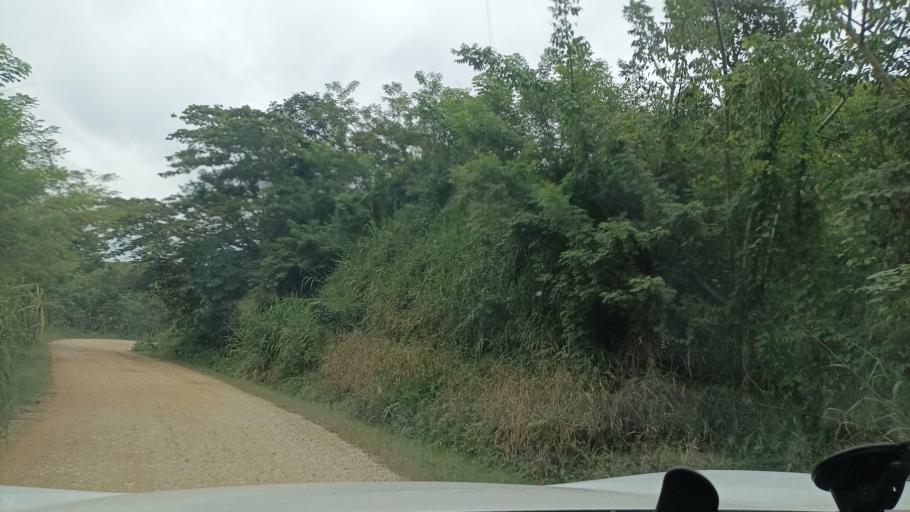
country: MX
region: Veracruz
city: Hidalgotitlan
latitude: 17.6209
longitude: -94.5150
